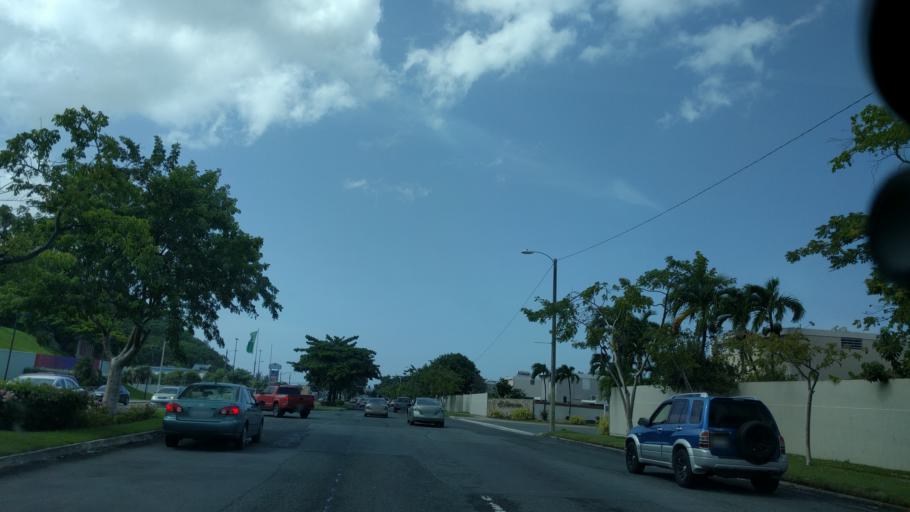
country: PR
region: Bayamon
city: Bayamon
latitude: 18.4110
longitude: -66.1595
